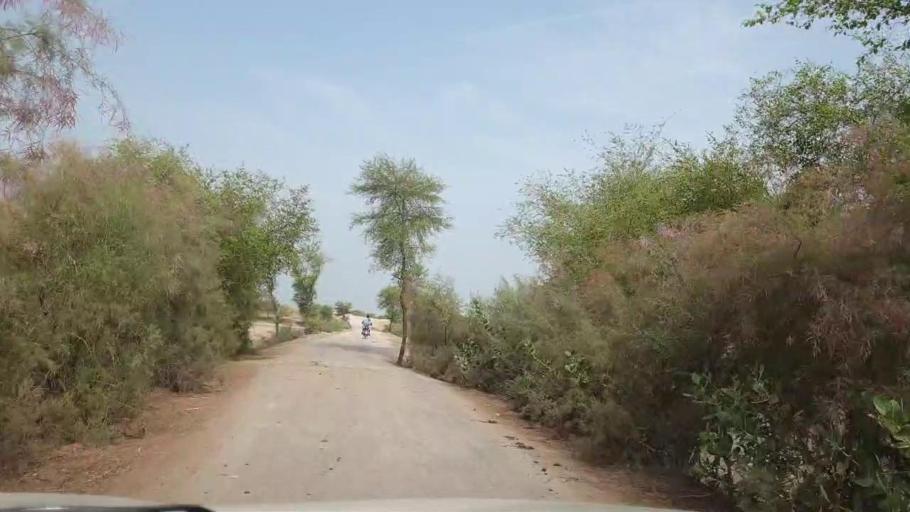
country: PK
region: Sindh
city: Dokri
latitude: 27.4049
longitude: 68.2451
